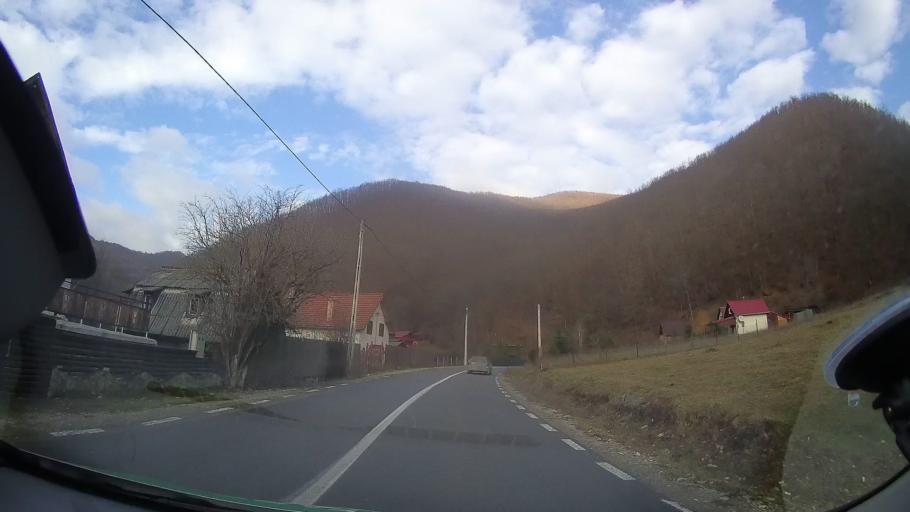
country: RO
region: Cluj
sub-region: Comuna Baisoara
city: Baisoara
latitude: 46.6109
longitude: 23.4125
